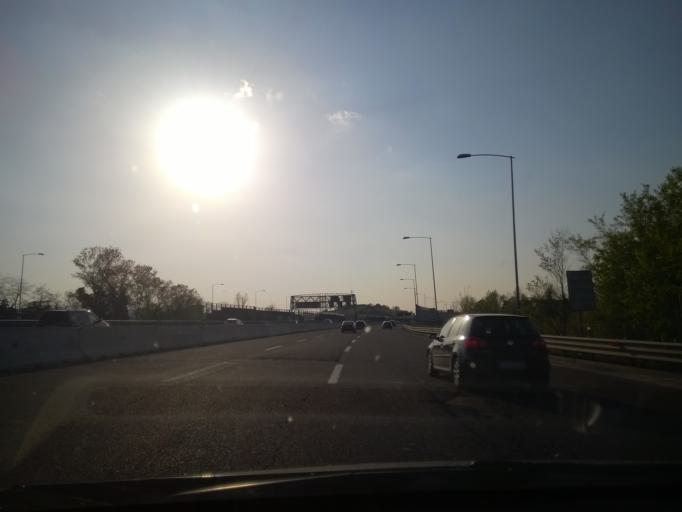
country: IT
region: Emilia-Romagna
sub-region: Provincia di Bologna
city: San Lazzaro
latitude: 44.4812
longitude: 11.4210
